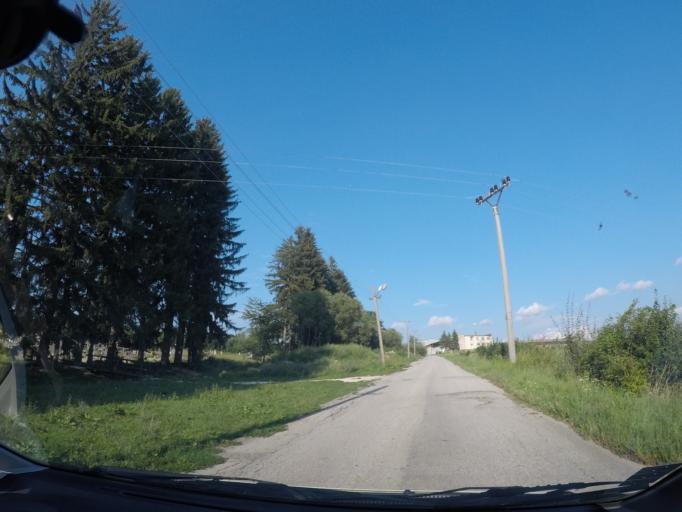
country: SK
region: Nitriansky
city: Bojnice
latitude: 48.8871
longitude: 18.6245
